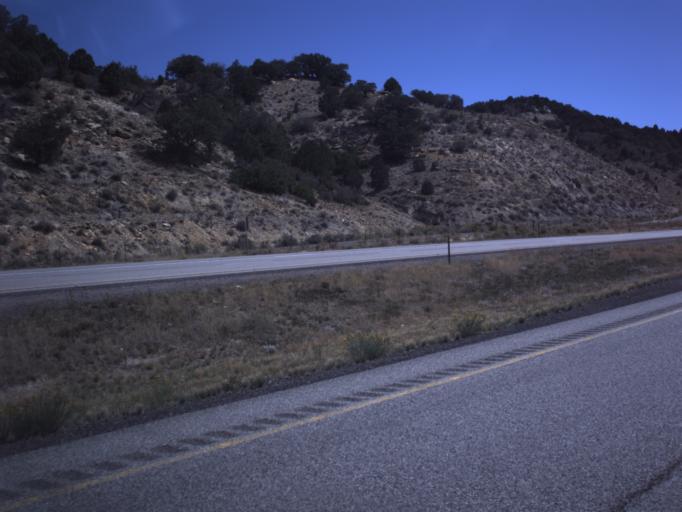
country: US
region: Utah
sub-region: Sevier County
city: Salina
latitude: 38.7974
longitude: -111.5115
